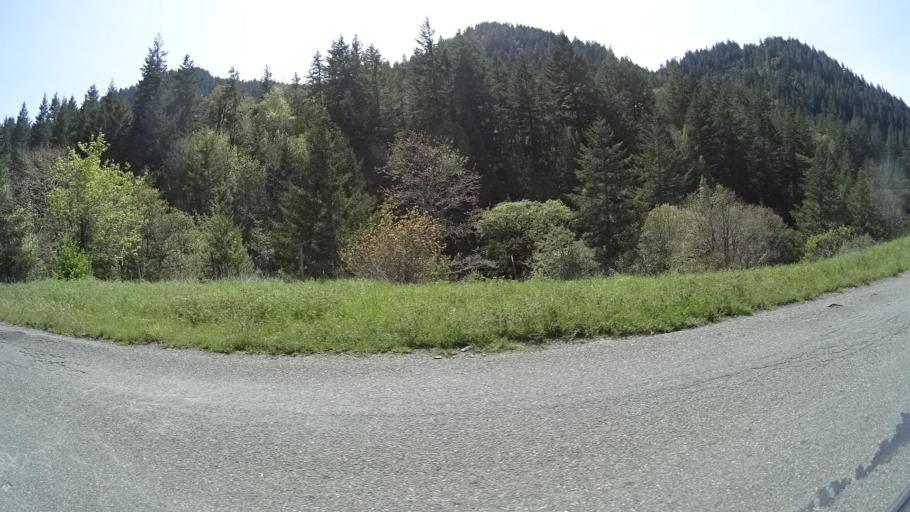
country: US
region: California
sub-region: Humboldt County
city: Rio Dell
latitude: 40.4515
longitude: -123.7993
